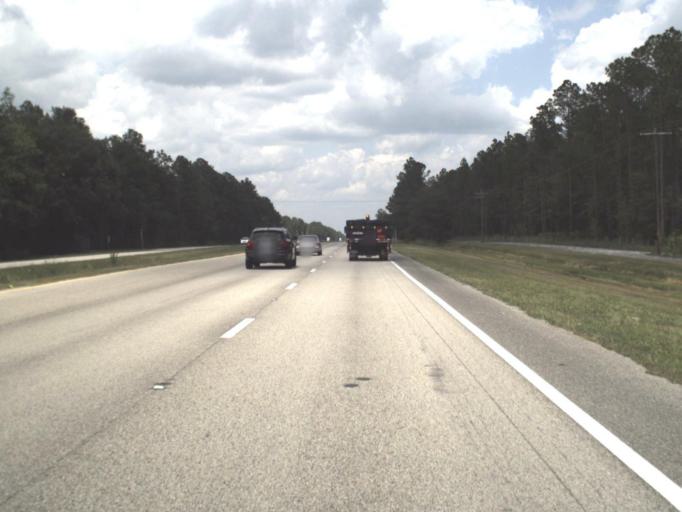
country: US
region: Florida
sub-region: Alachua County
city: Waldo
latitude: 29.7446
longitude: -82.2294
